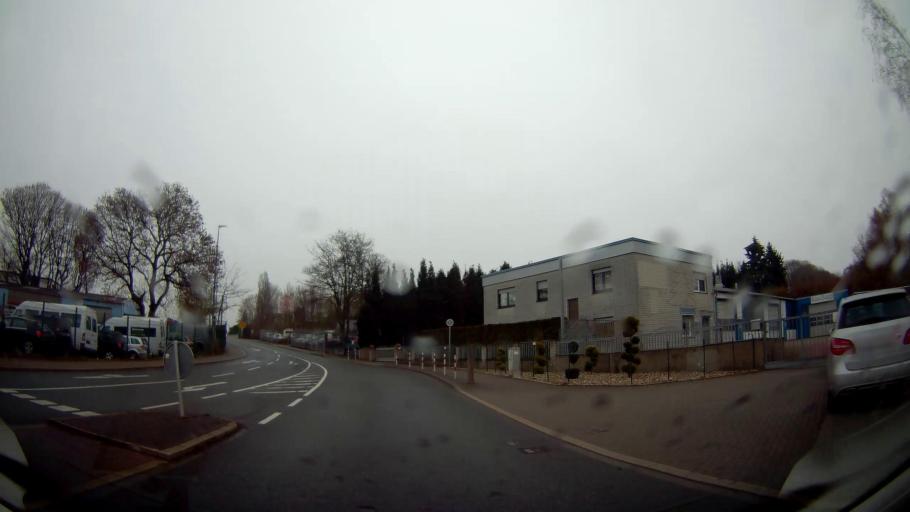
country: DE
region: North Rhine-Westphalia
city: Castrop-Rauxel
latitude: 51.5226
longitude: 7.2991
